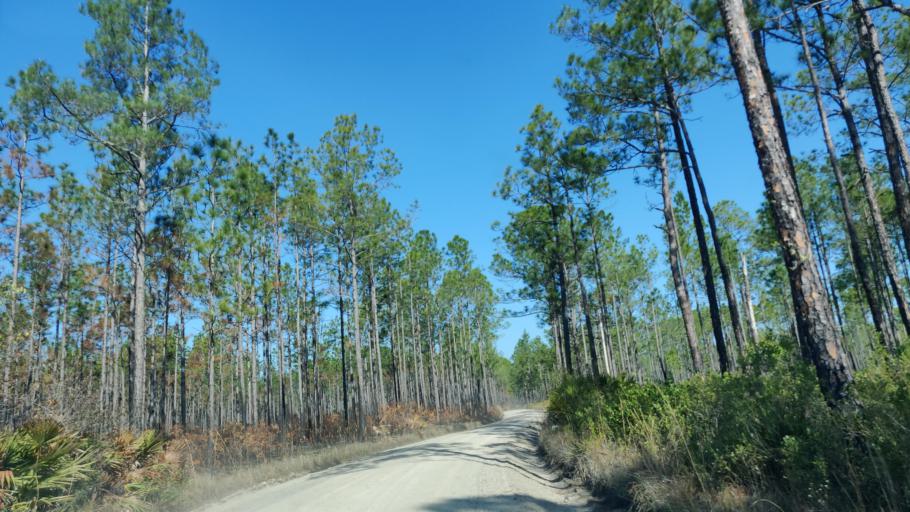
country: US
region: Florida
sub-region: Clay County
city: Middleburg
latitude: 30.1613
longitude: -81.9467
